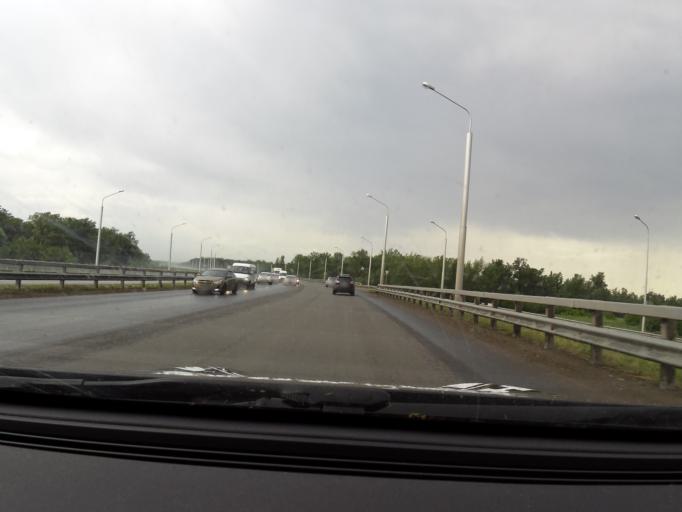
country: RU
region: Bashkortostan
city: Ufa
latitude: 54.7769
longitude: 55.9485
